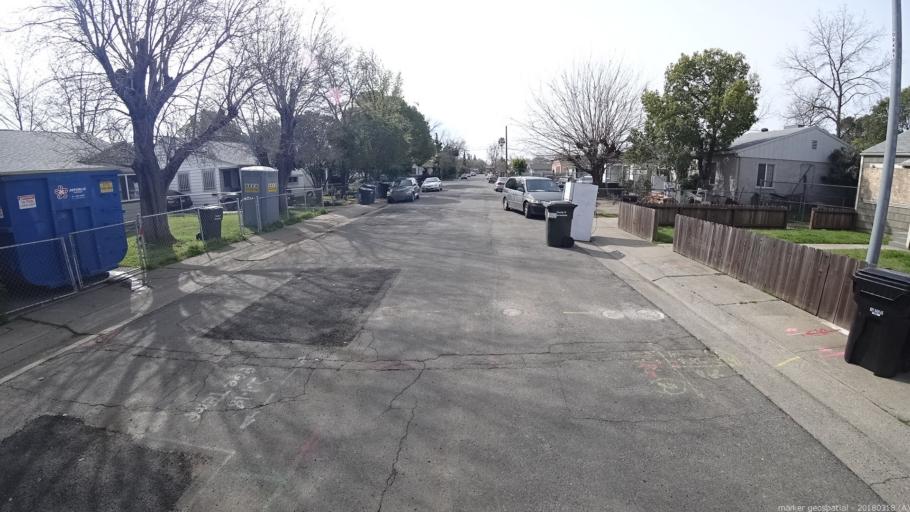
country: US
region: California
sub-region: Sacramento County
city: Parkway
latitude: 38.5374
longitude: -121.4508
